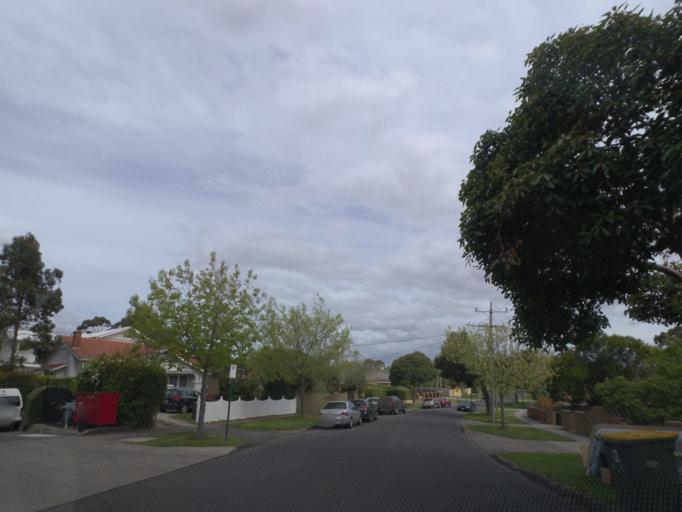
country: AU
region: Victoria
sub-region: Whitehorse
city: Surrey Hills
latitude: -37.8283
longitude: 145.1042
